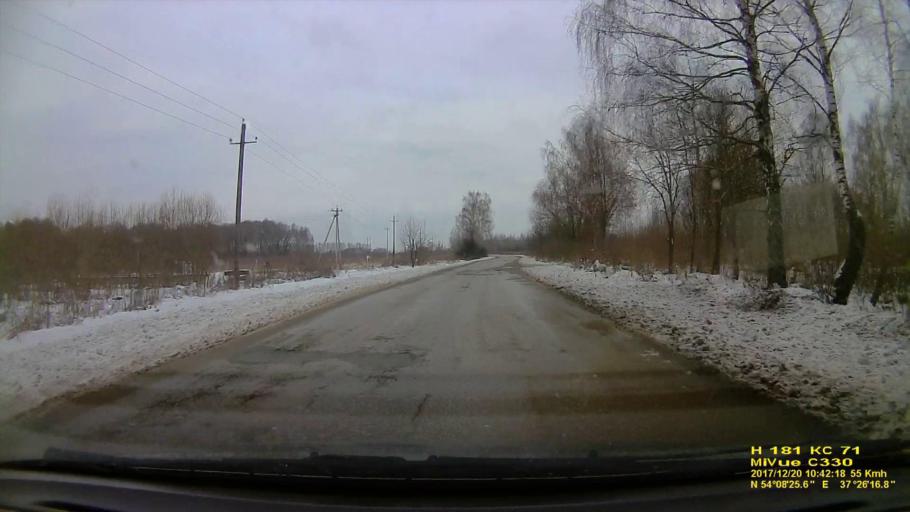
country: RU
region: Tula
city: Kosaya Gora
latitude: 54.1405
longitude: 37.4380
